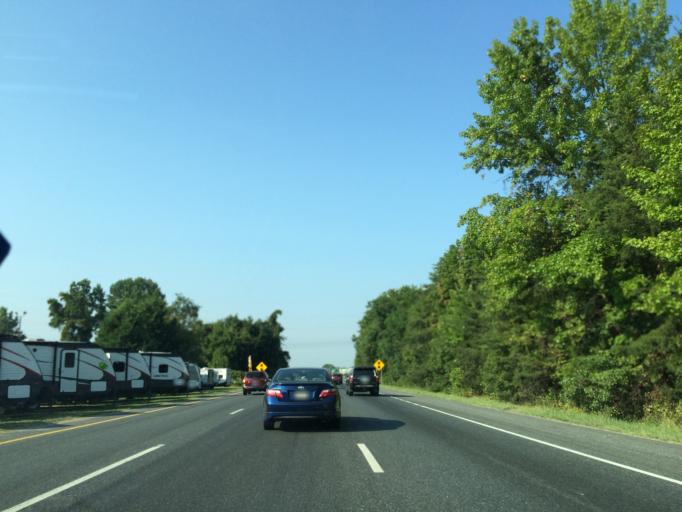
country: US
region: Maryland
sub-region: Anne Arundel County
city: Gambrills
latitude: 39.0431
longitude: -76.6701
